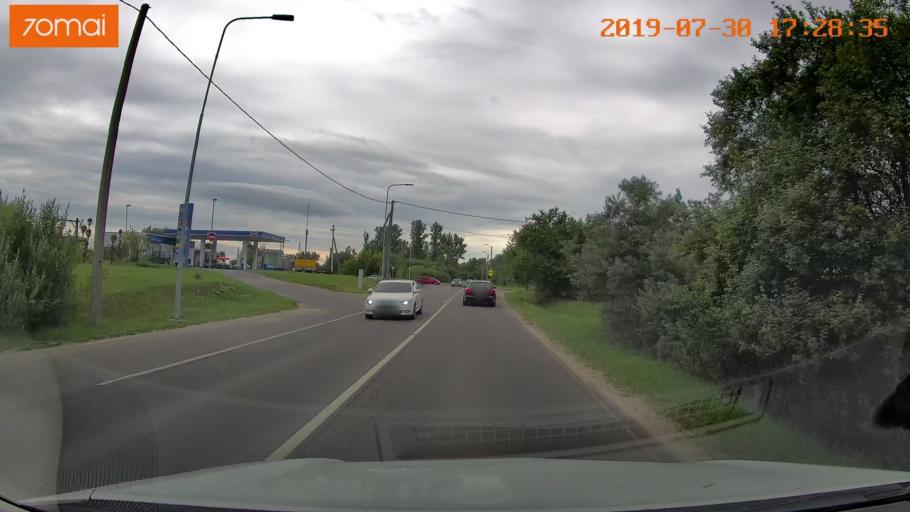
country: LT
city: Skaidiskes
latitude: 54.7047
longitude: 25.4164
